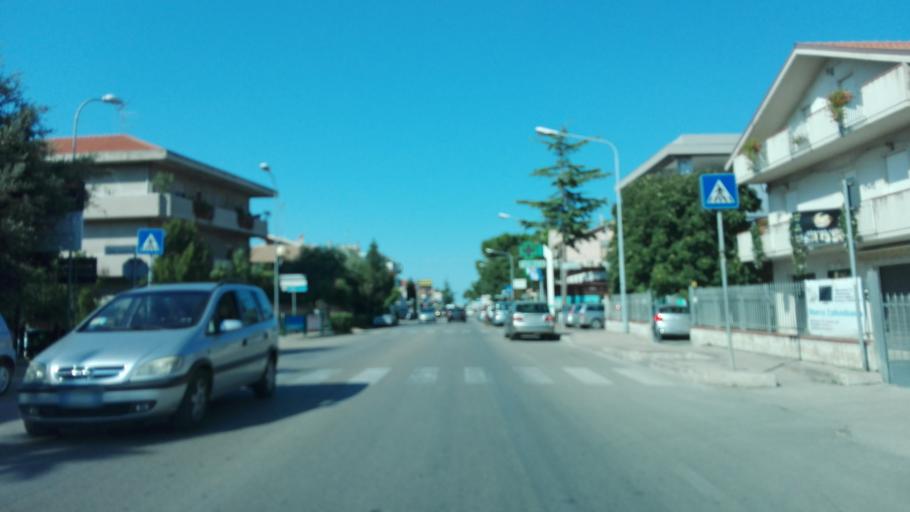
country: IT
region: Abruzzo
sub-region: Provincia di Pescara
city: Montesilvano Marina
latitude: 42.4994
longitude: 14.1313
